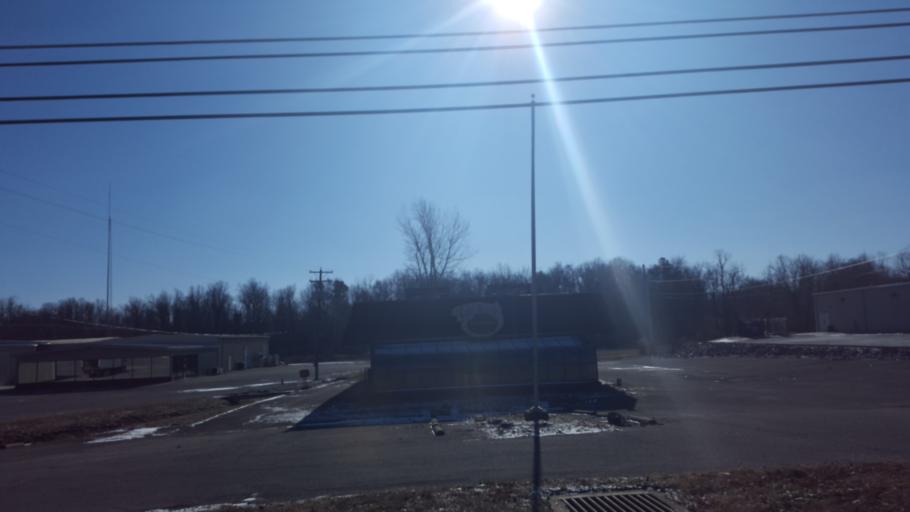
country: US
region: Kentucky
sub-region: Crittenden County
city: Marion
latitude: 37.3413
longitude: -88.0749
